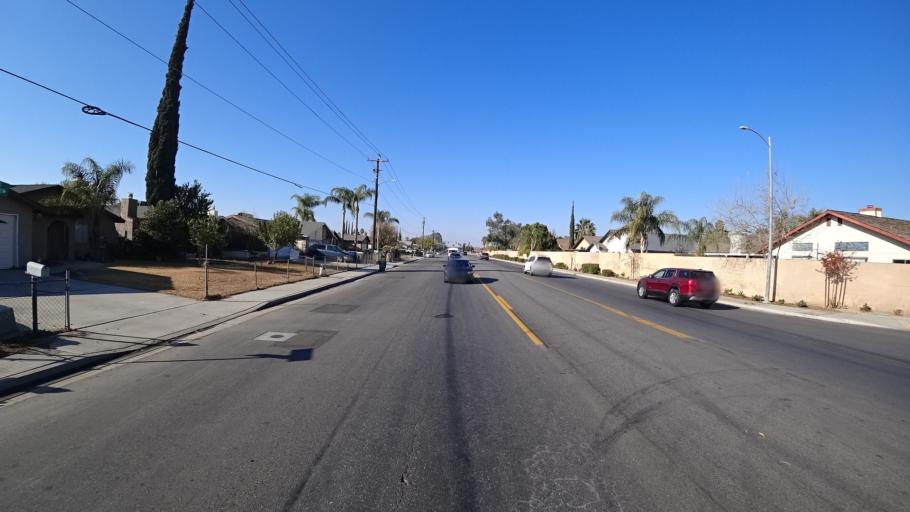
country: US
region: California
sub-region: Kern County
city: Greenfield
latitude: 35.3104
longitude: -119.0276
